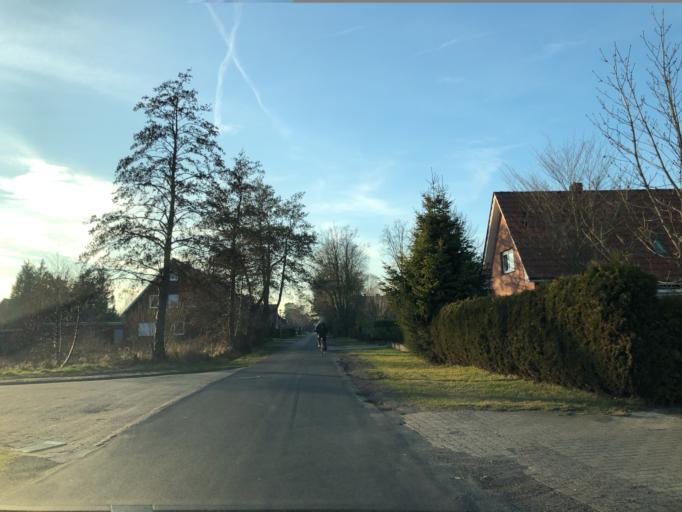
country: DE
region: Lower Saxony
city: Papenburg
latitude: 53.0682
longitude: 7.4051
